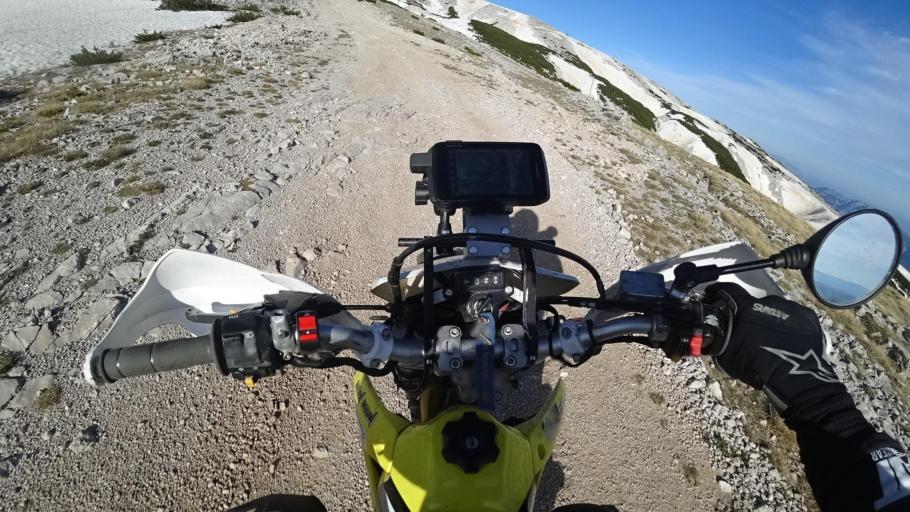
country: BA
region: Federation of Bosnia and Herzegovina
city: Kocerin
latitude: 43.5998
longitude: 17.5448
